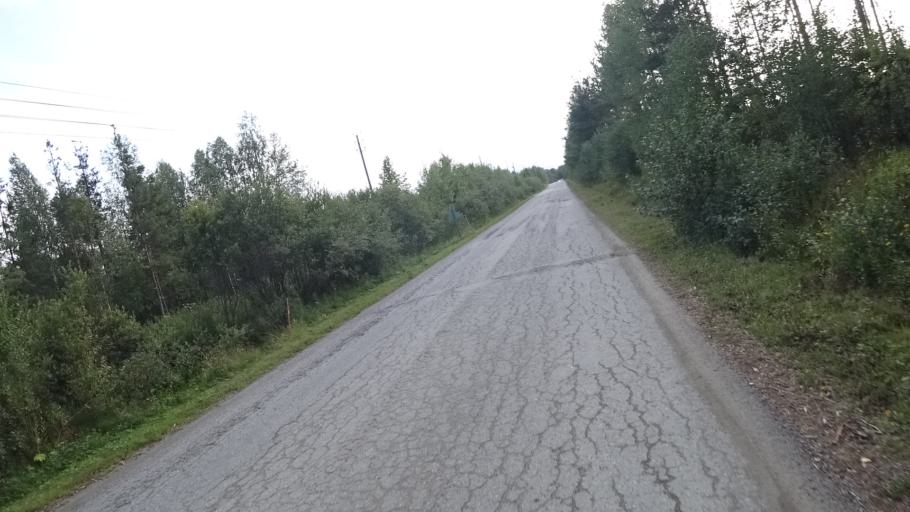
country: FI
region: North Karelia
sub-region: Joensuu
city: Ilomantsi
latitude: 62.6685
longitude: 30.9517
